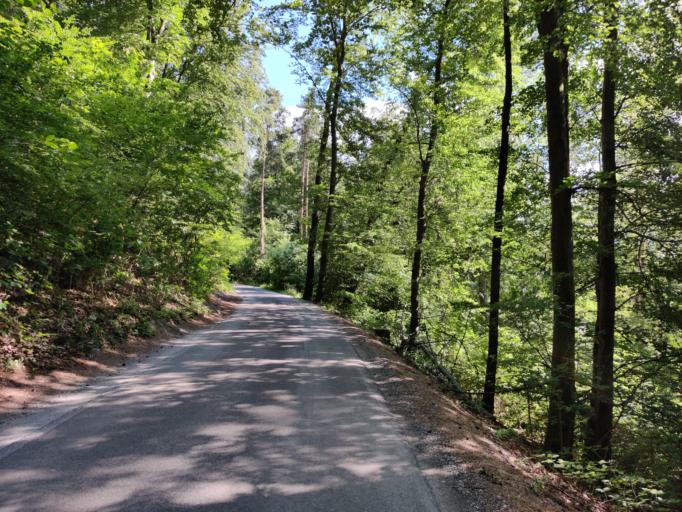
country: AT
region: Styria
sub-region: Graz Stadt
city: Wetzelsdorf
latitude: 47.0363
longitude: 15.3672
